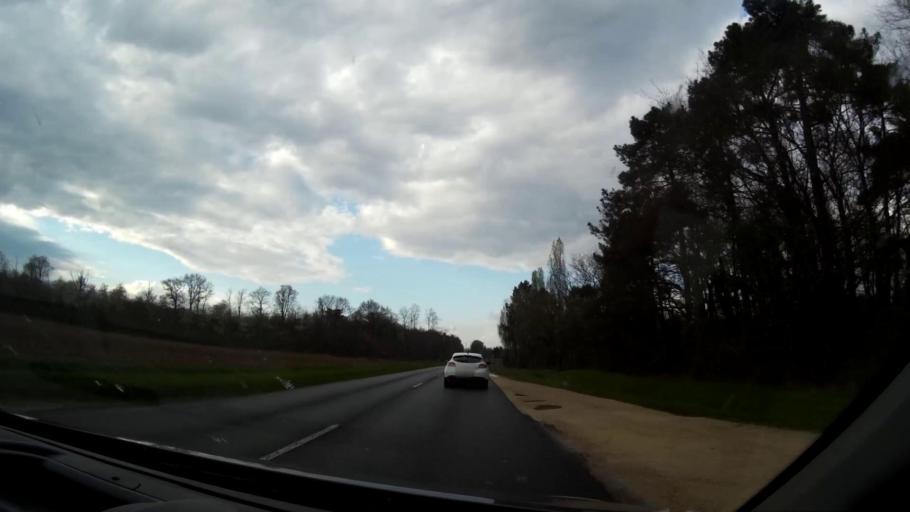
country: FR
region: Centre
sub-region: Departement du Loir-et-Cher
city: Cormeray
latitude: 47.4608
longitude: 1.4251
